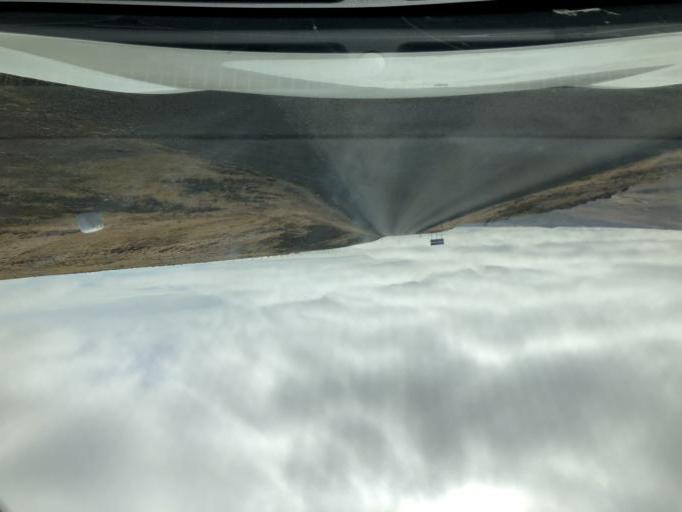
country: IS
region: West
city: Borgarnes
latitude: 65.2222
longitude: -21.1164
